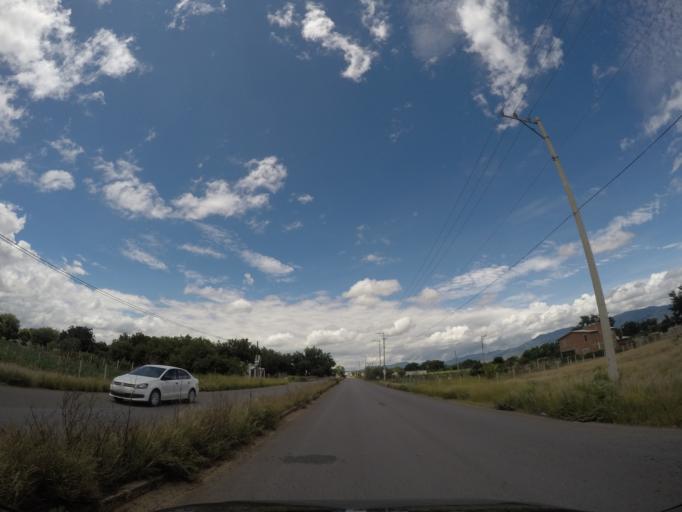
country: MX
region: Oaxaca
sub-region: Santa Cruz Xoxocotlan
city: San Isidro Monjas
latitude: 16.9872
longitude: -96.7460
